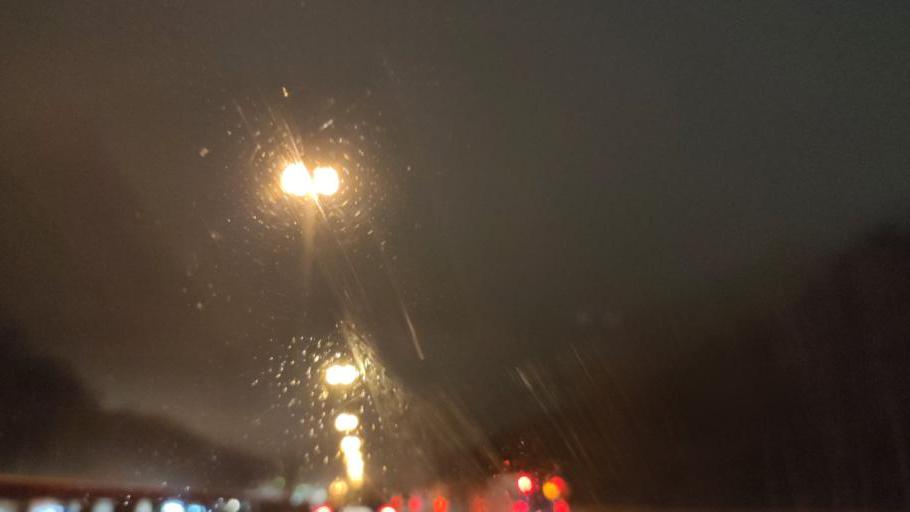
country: RU
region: Moscow
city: Solntsevo
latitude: 55.6218
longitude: 37.4027
